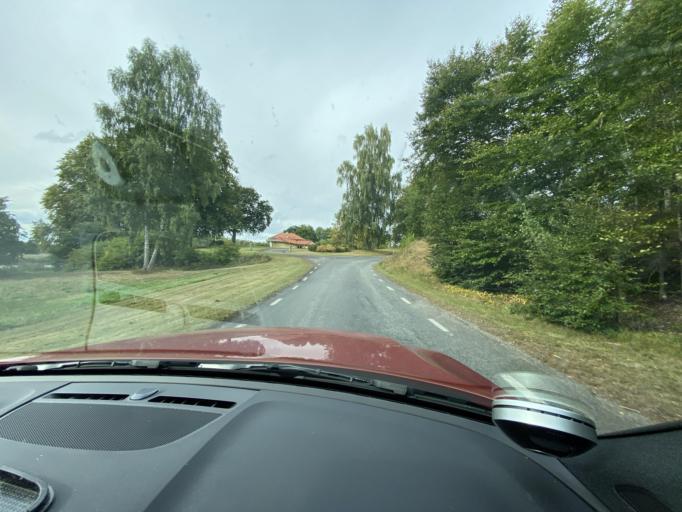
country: SE
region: Skane
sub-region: Hassleholms Kommun
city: Bjarnum
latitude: 56.3524
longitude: 13.7024
